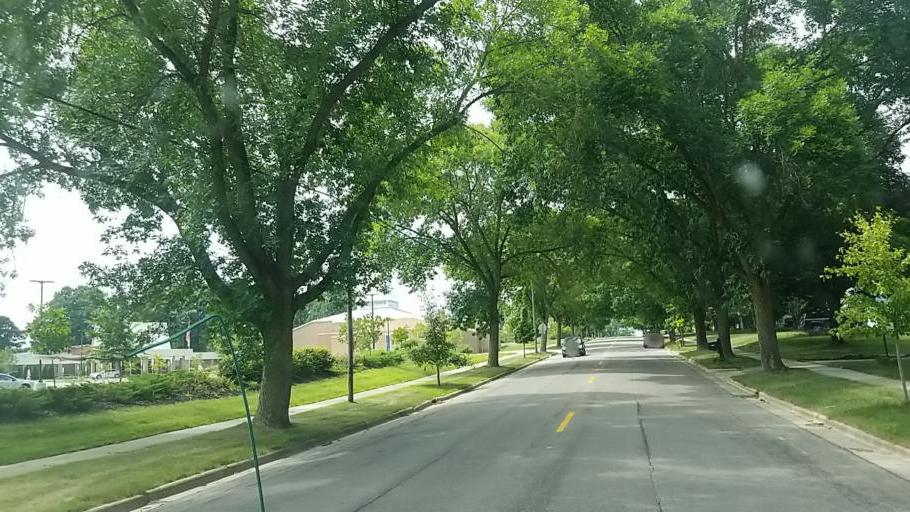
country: US
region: Michigan
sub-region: Kent County
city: Walker
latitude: 42.9961
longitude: -85.7297
